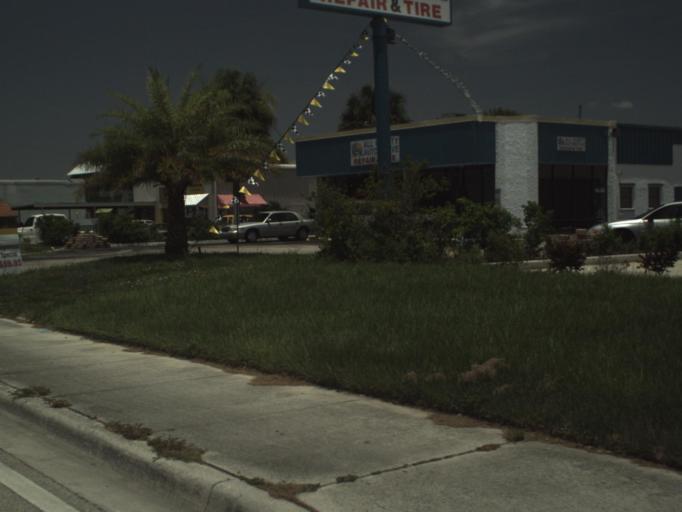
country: US
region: Florida
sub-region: Martin County
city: Stuart
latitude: 27.1756
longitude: -80.2409
